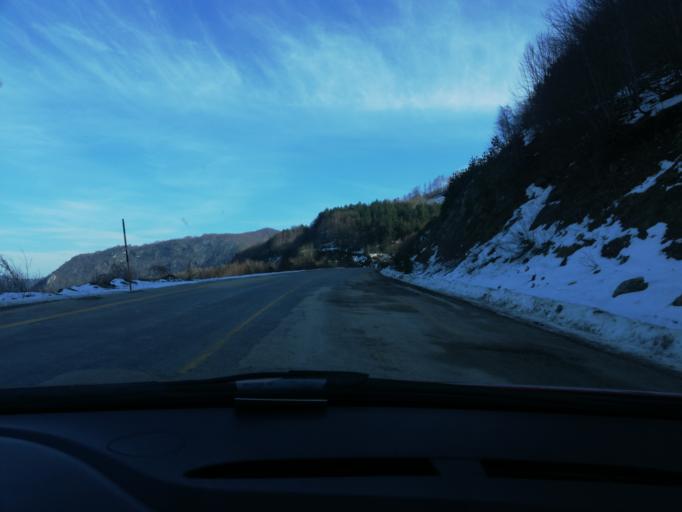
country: TR
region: Kastamonu
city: Cide
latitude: 41.8587
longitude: 33.0603
